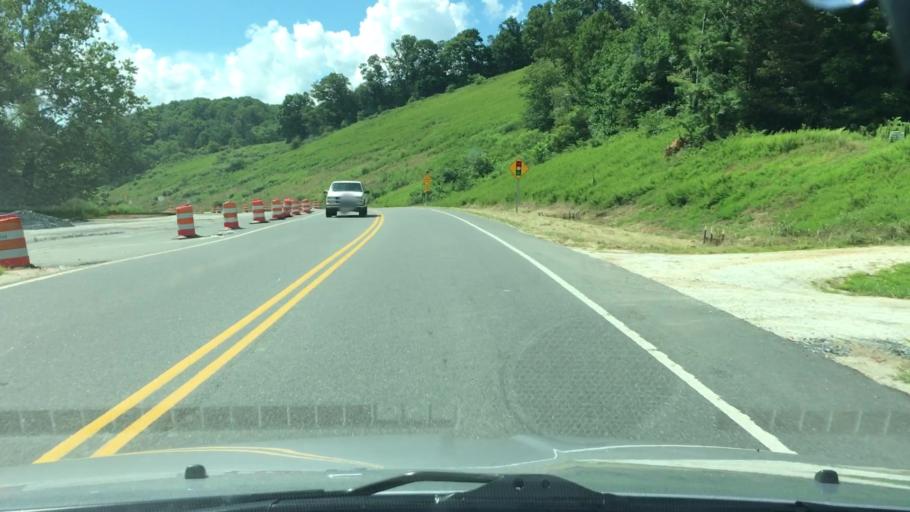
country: US
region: North Carolina
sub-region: Yancey County
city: Burnsville
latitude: 35.9101
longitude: -82.2204
